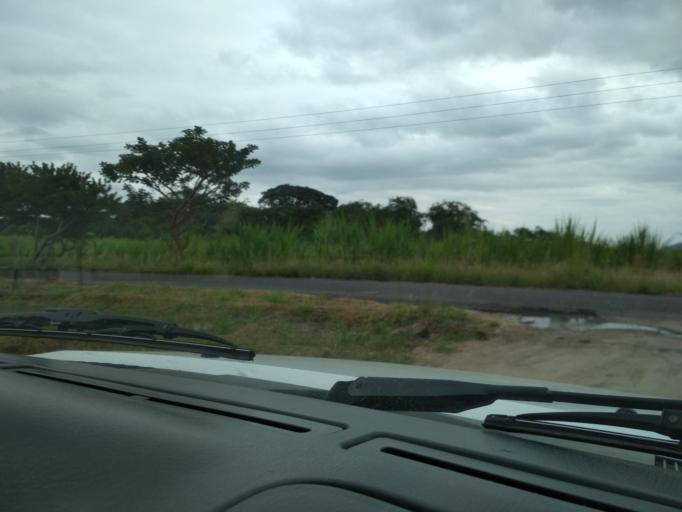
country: MX
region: Veracruz
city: El Castillo
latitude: 19.5849
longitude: -96.8259
